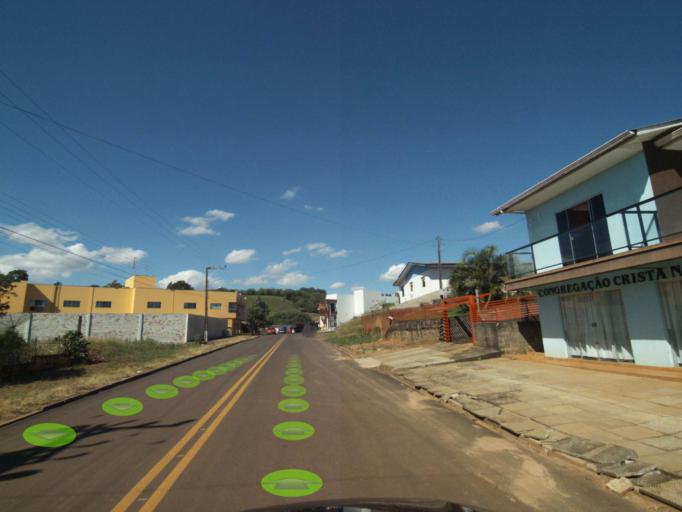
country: BR
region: Parana
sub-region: Coronel Vivida
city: Coronel Vivida
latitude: -26.1437
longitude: -52.3841
